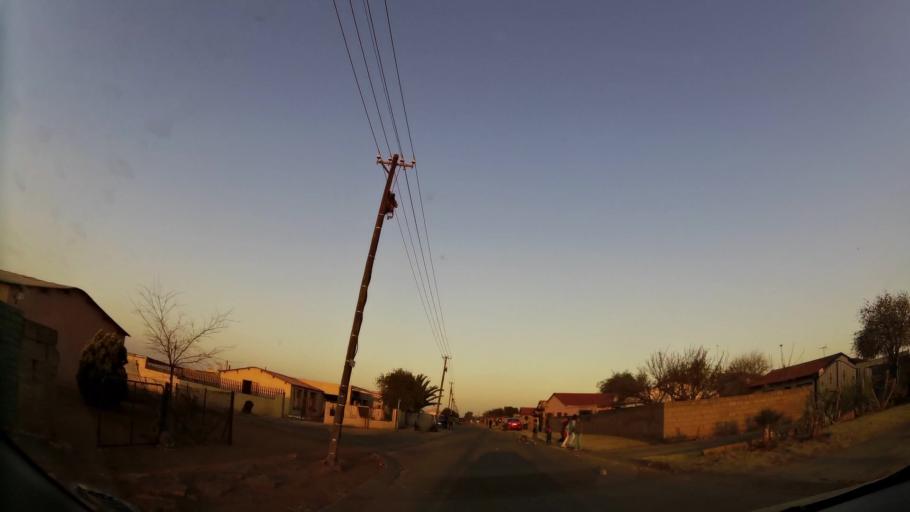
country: ZA
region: Gauteng
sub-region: West Rand District Municipality
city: Randfontein
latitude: -26.2005
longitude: 27.7113
